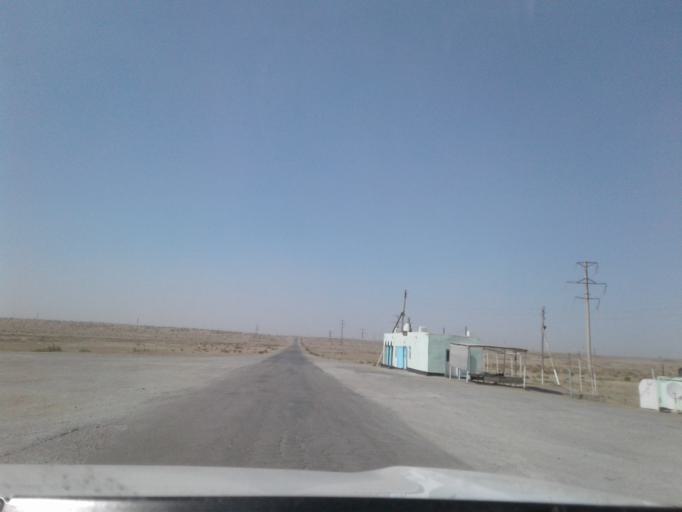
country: TM
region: Balkan
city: Gumdag
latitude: 39.1158
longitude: 54.5828
